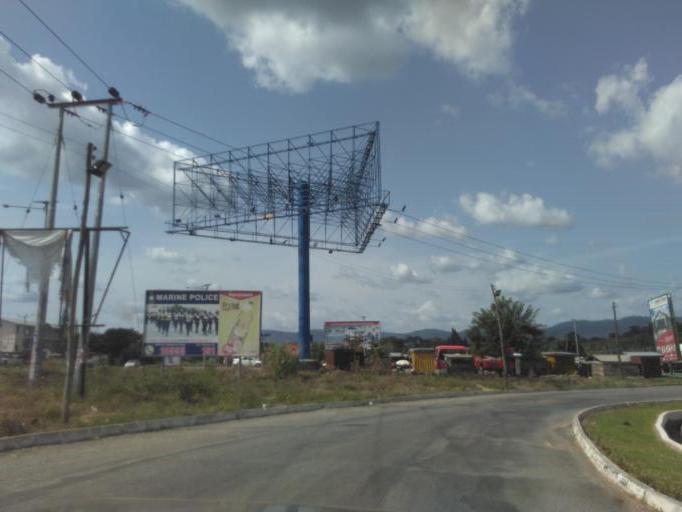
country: GH
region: Eastern
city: Begoro
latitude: 6.2923
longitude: -0.4744
